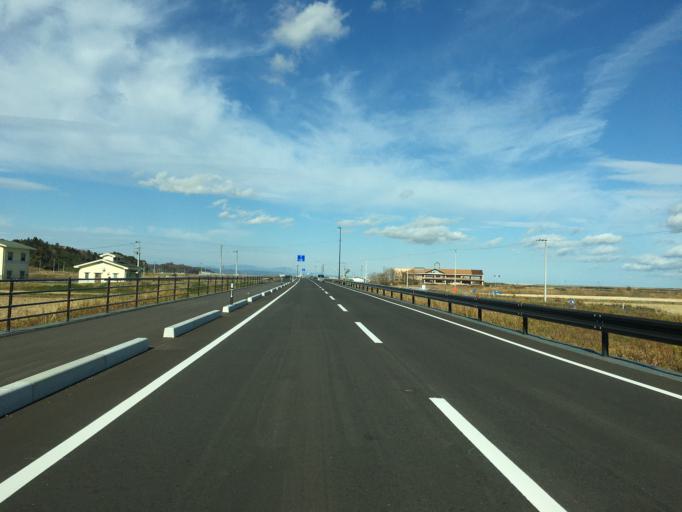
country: JP
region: Miyagi
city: Watari
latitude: 37.9125
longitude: 140.9183
